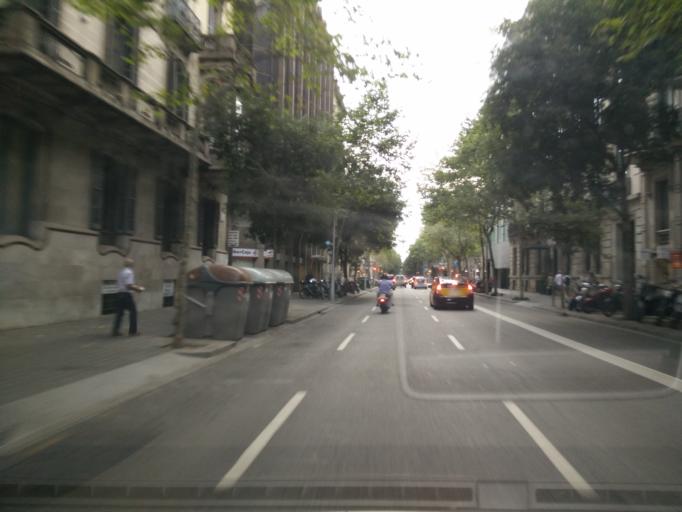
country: ES
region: Catalonia
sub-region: Provincia de Barcelona
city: Eixample
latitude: 41.3947
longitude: 2.1638
